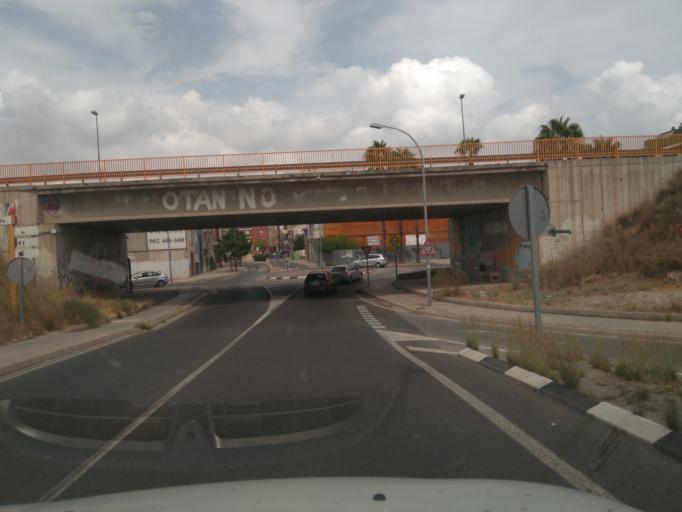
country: ES
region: Valencia
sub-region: Provincia de Valencia
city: Alzira
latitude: 39.1444
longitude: -0.4377
